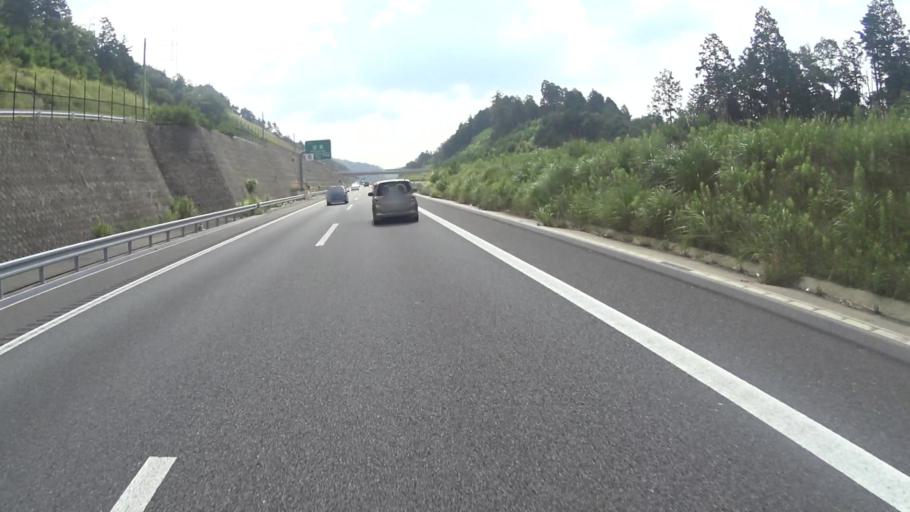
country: JP
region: Shiga Prefecture
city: Minakuchicho-matoba
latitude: 34.9281
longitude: 136.0693
